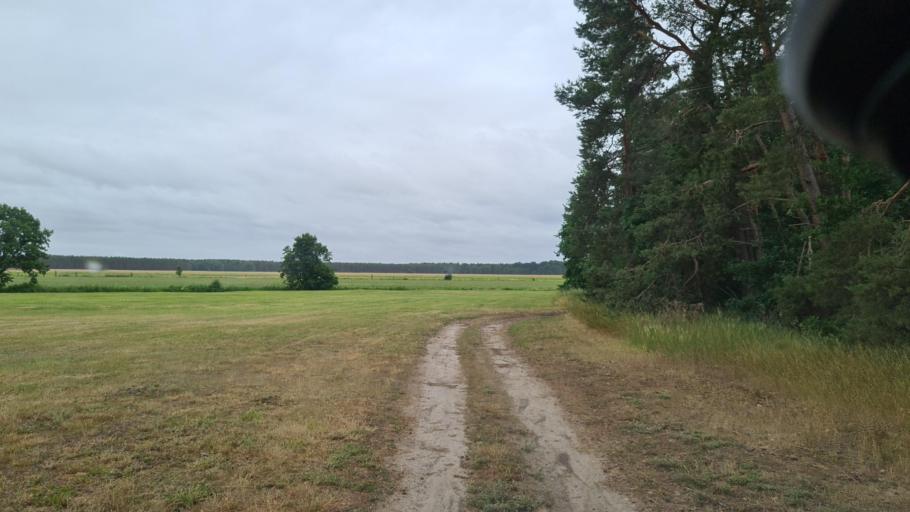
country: DE
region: Saxony-Anhalt
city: Holzdorf
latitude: 51.7975
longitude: 13.1883
